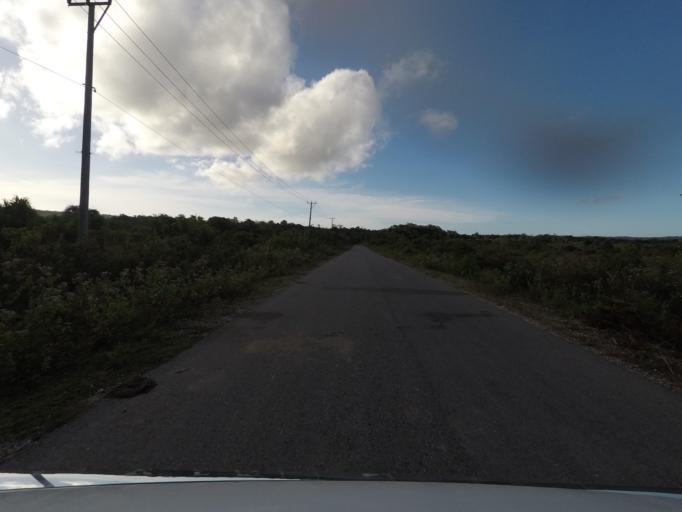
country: TL
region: Lautem
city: Lospalos
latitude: -8.4219
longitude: 127.0049
